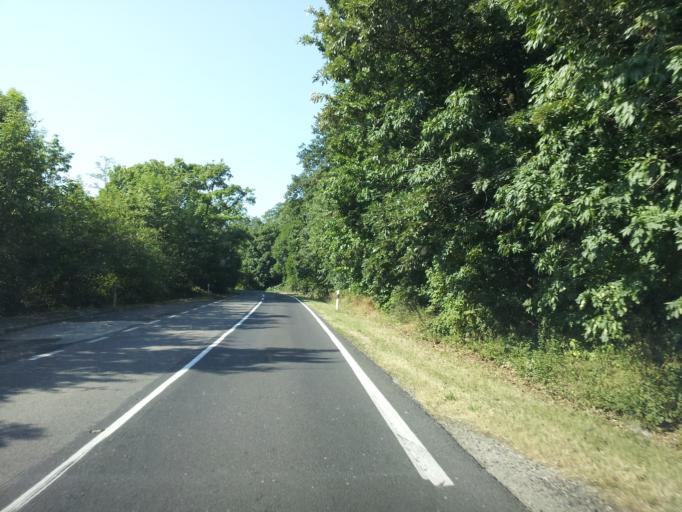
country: HU
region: Fejer
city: Bicske
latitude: 47.4091
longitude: 18.5838
